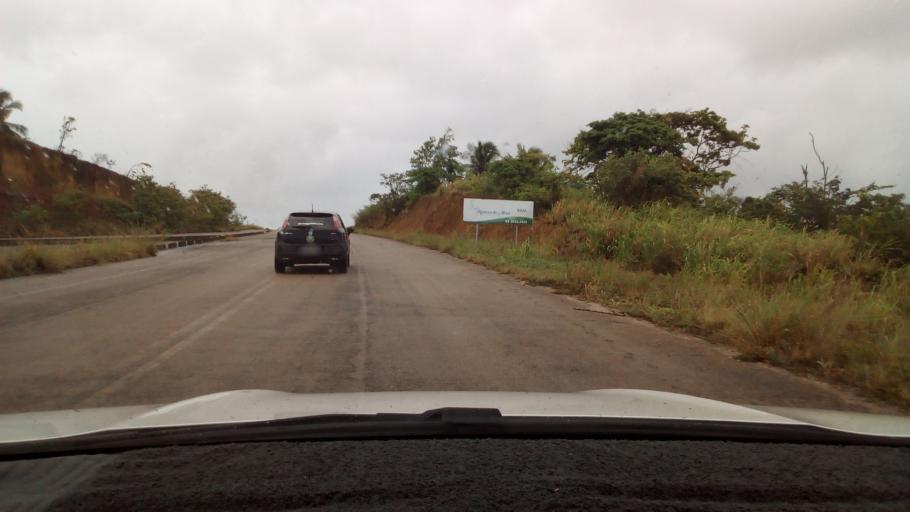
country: BR
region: Paraiba
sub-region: Pitimbu
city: Pitimbu
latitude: -7.4206
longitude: -34.8317
